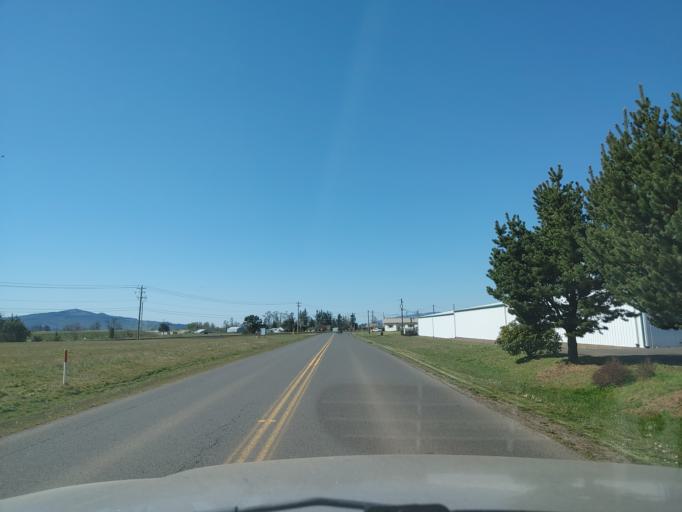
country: US
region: Oregon
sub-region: Tillamook County
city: Tillamook
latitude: 45.4240
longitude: -123.7994
